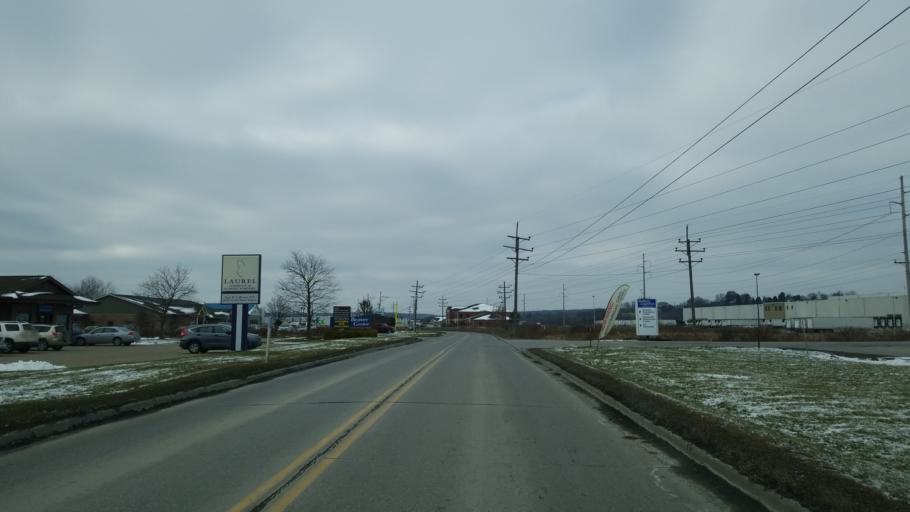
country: US
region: Pennsylvania
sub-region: Clearfield County
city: DuBois
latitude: 41.1202
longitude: -78.7339
